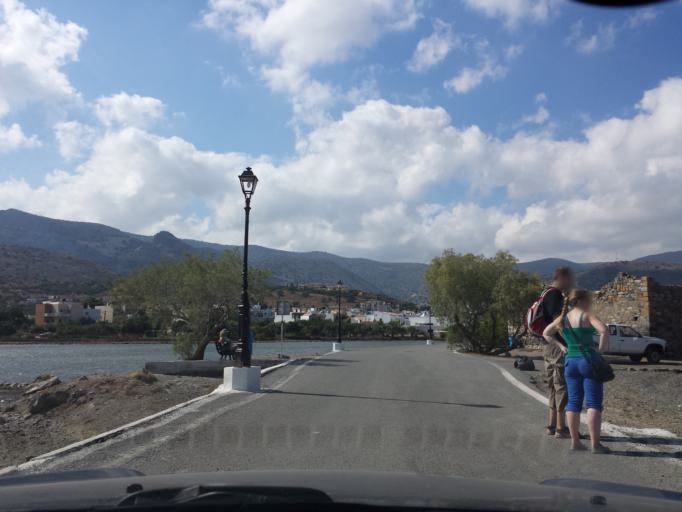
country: GR
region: Crete
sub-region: Nomos Lasithiou
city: Skhisma
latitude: 35.2571
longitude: 25.7317
